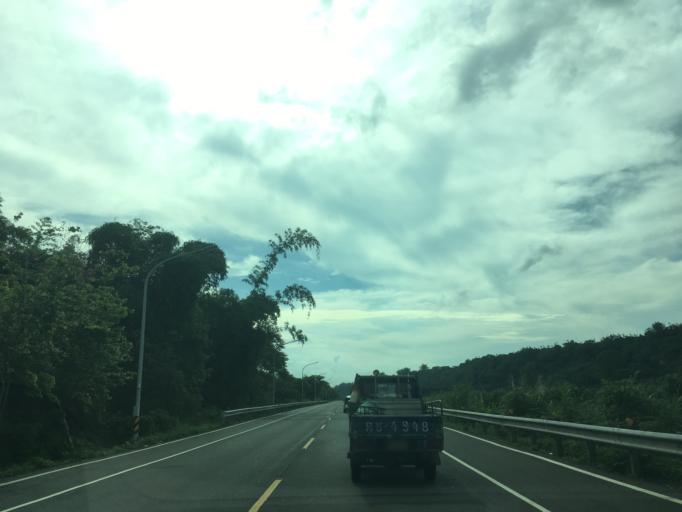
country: TW
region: Taiwan
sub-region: Chiayi
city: Jiayi Shi
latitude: 23.4483
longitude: 120.5769
